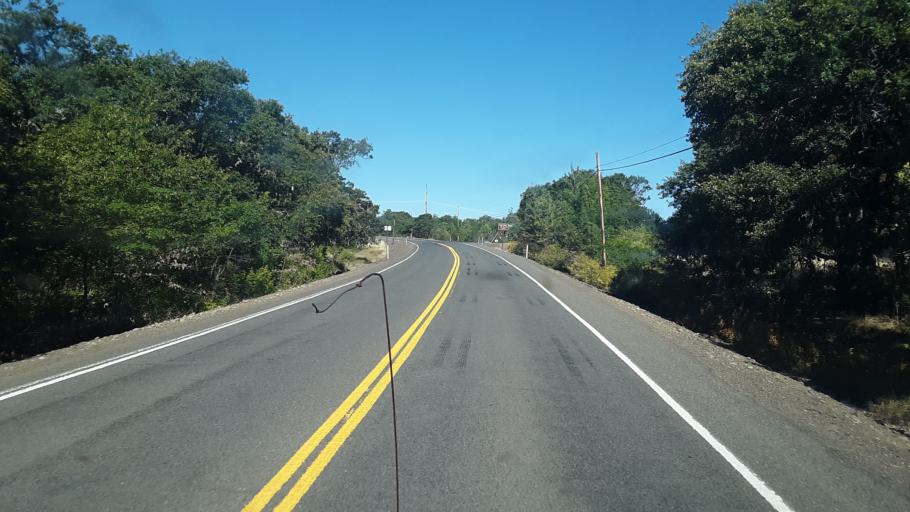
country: US
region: Oregon
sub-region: Jackson County
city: Eagle Point
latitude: 42.5256
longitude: -122.8442
